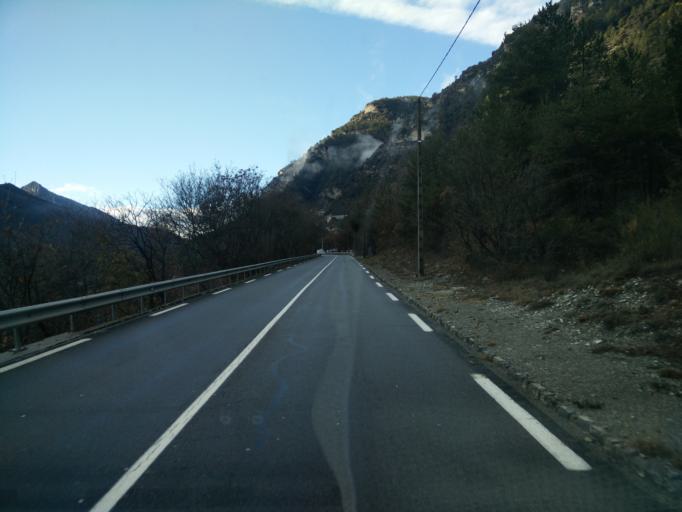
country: FR
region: Provence-Alpes-Cote d'Azur
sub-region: Departement des Alpes-Maritimes
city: Puget-Theniers
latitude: 43.9461
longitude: 7.0209
